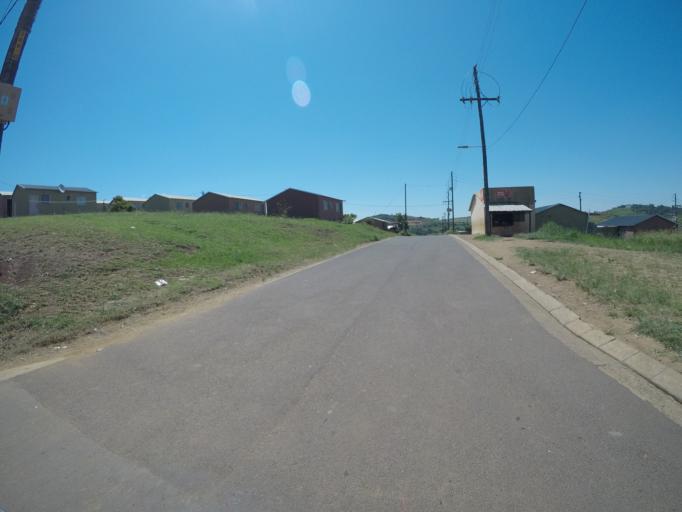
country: ZA
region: KwaZulu-Natal
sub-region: uThungulu District Municipality
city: Empangeni
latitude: -28.7630
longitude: 31.8766
